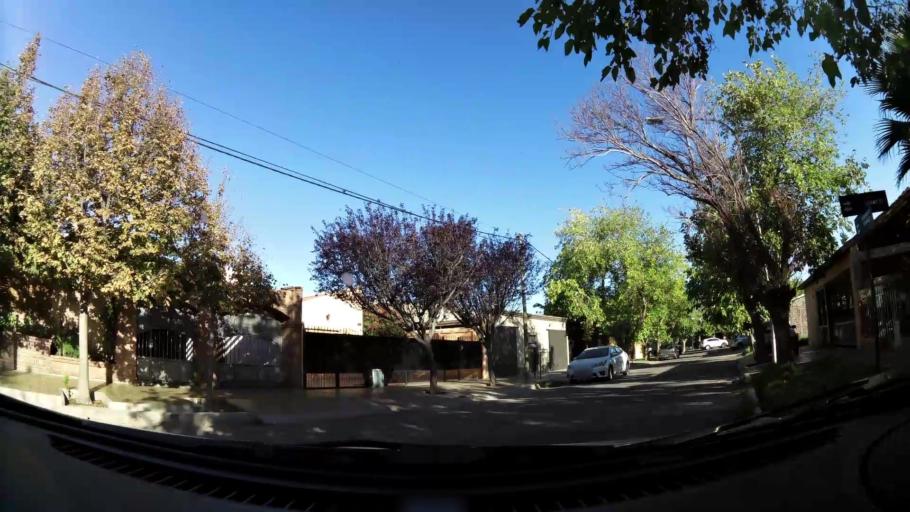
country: AR
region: San Juan
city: Villa Krause
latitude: -31.5615
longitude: -68.5162
